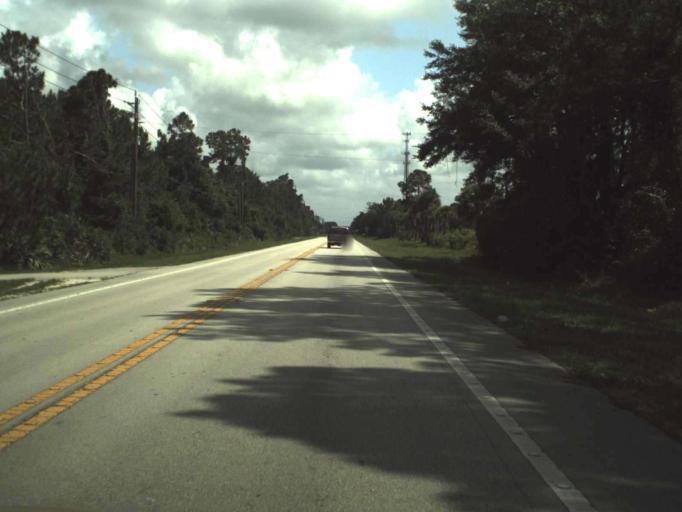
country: US
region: Florida
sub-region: Volusia County
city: Samsula-Spruce Creek
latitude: 29.0032
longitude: -81.0701
